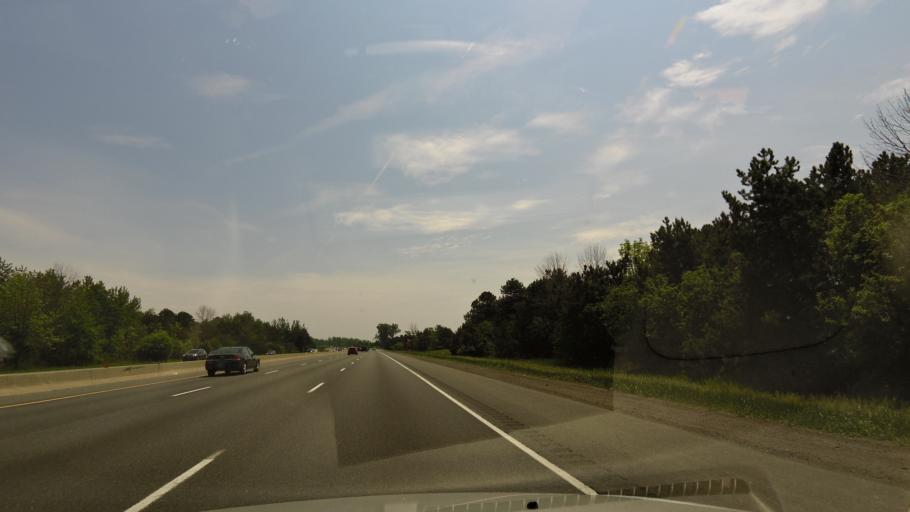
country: CA
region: Ontario
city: Oshawa
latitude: 43.8809
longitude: -78.8064
